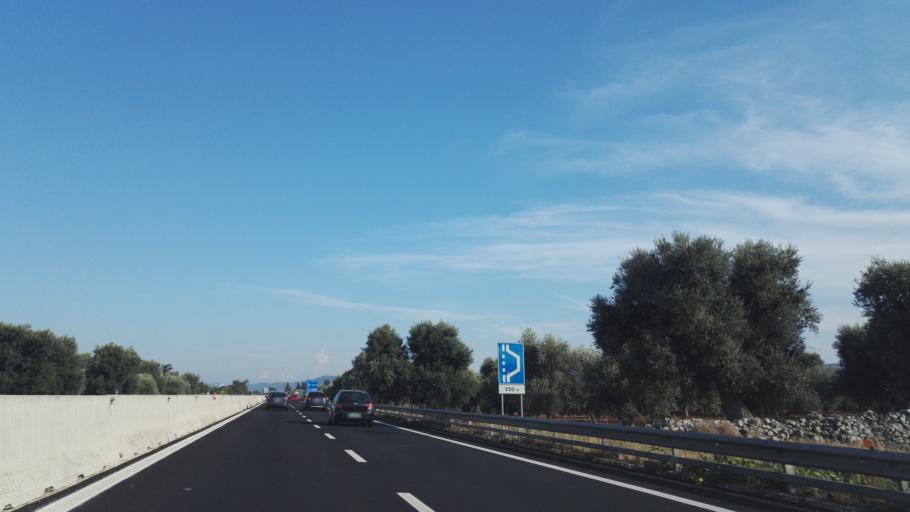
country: IT
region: Apulia
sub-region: Provincia di Brindisi
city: Fasano
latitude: 40.8462
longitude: 17.3627
